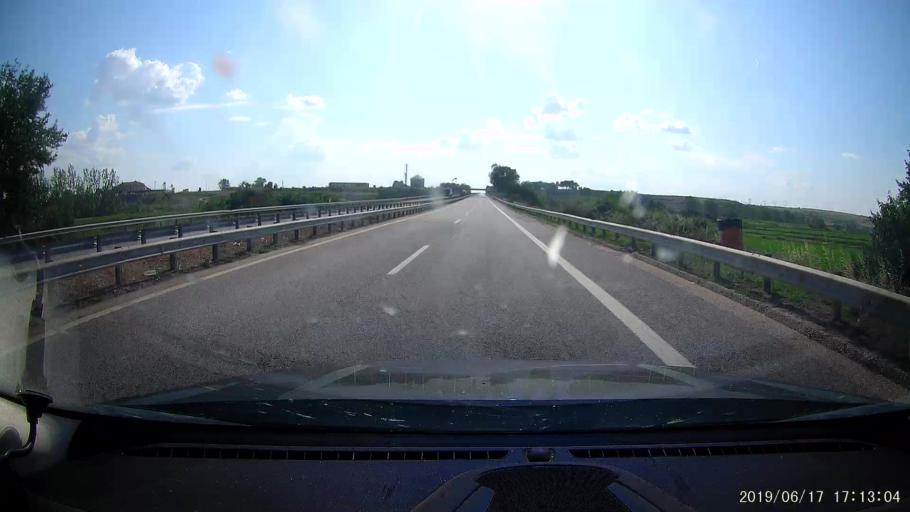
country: TR
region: Edirne
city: Edirne
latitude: 41.7013
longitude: 26.5474
